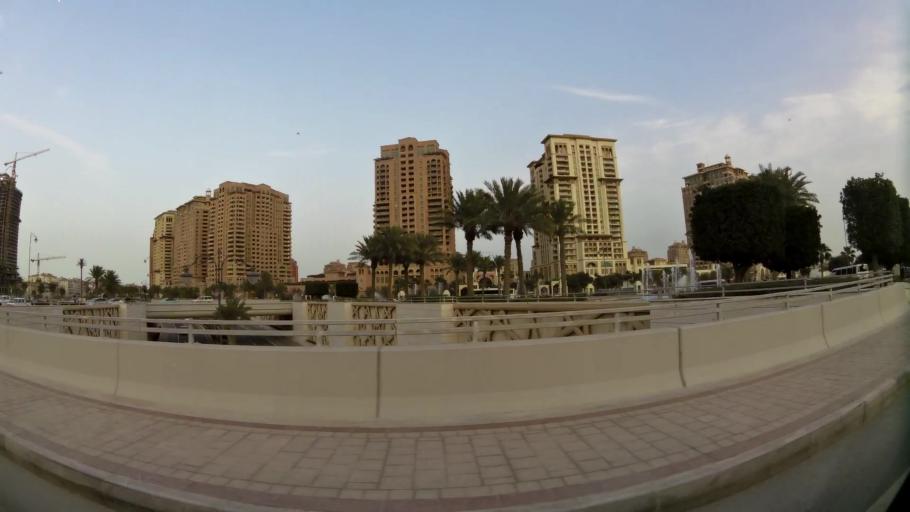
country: QA
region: Baladiyat ad Dawhah
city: Doha
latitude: 25.3717
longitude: 51.5364
